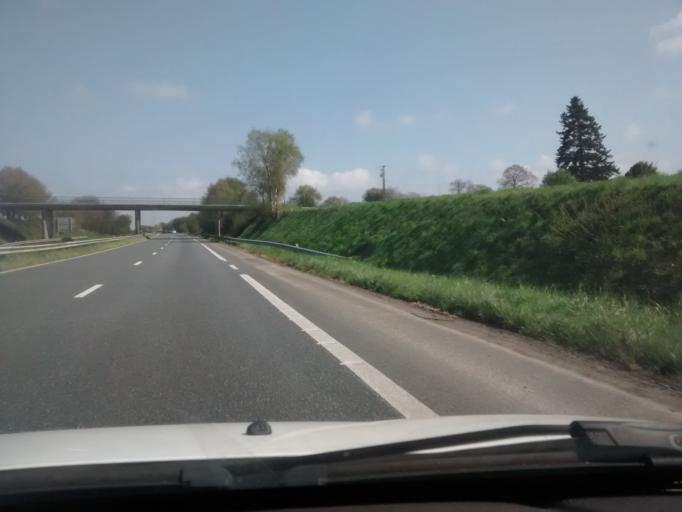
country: FR
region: Brittany
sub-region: Departement des Cotes-d'Armor
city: Plouagat
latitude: 48.5305
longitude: -2.9967
